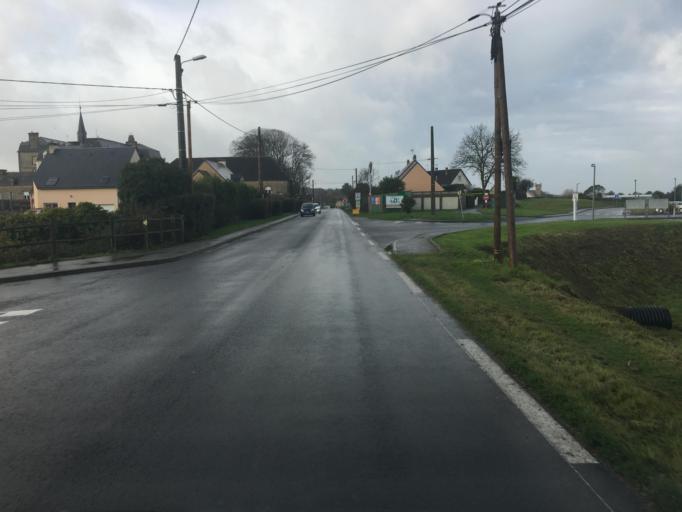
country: FR
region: Lower Normandy
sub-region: Departement de la Manche
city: Saint-Pierre-Eglise
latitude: 49.6671
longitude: -1.3934
